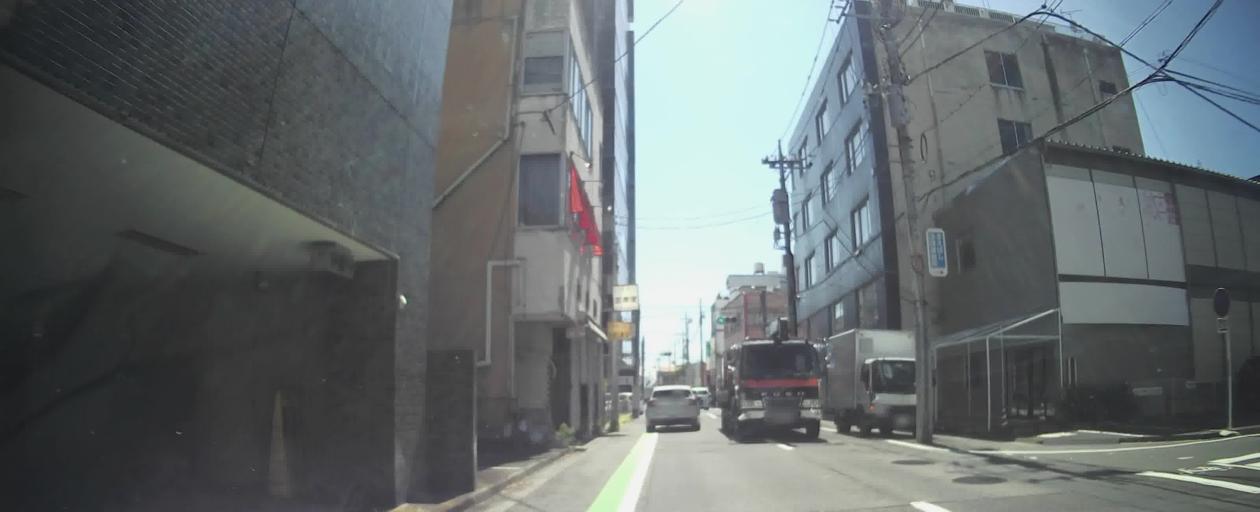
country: JP
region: Gunma
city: Maebashi-shi
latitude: 36.3914
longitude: 139.0652
